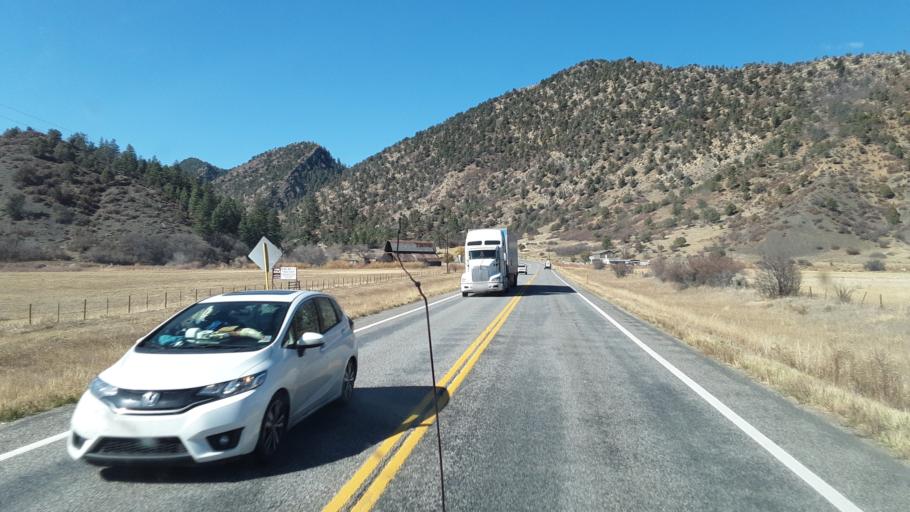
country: US
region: Colorado
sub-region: La Plata County
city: Bayfield
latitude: 37.2255
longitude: -107.3435
